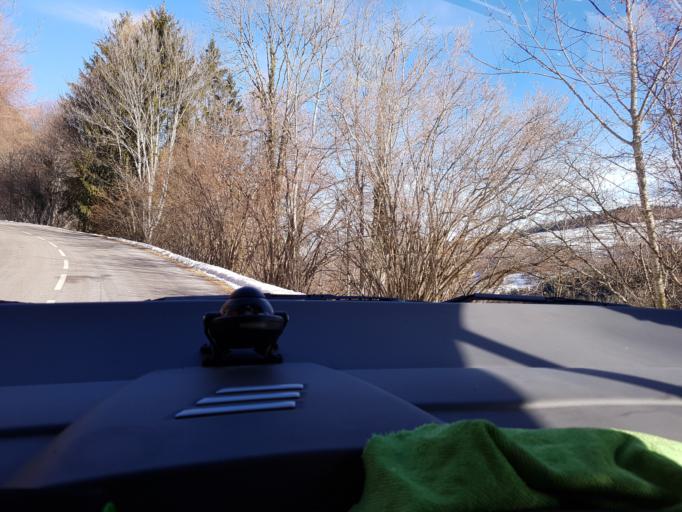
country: FR
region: Alsace
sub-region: Departement du Haut-Rhin
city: Metzeral
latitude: 47.9913
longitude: 7.0662
